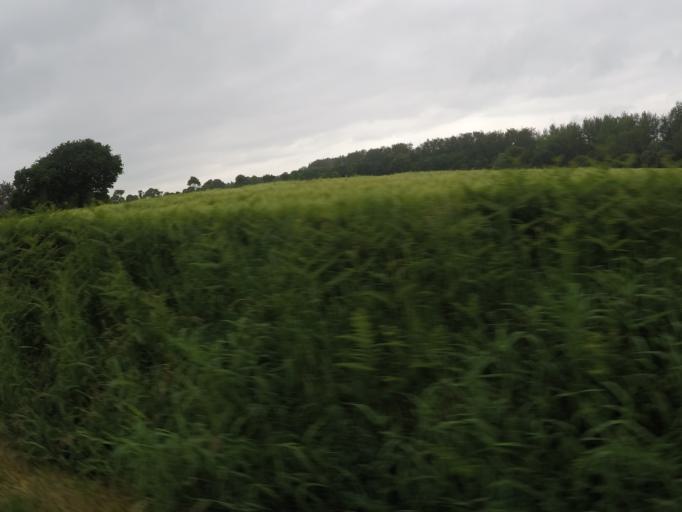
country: FR
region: Brittany
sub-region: Departement des Cotes-d'Armor
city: Goudelin
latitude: 48.6301
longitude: -3.0451
